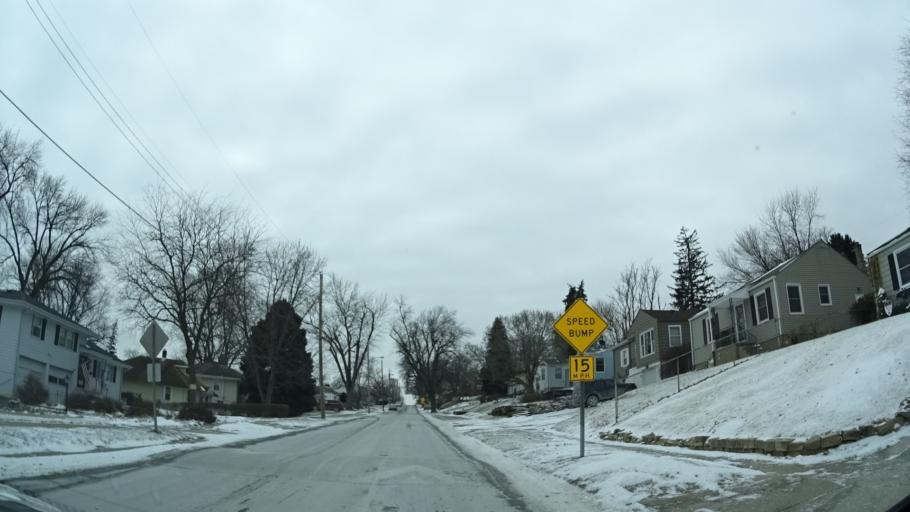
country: US
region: Nebraska
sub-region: Douglas County
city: Omaha
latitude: 41.2368
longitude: -95.9855
